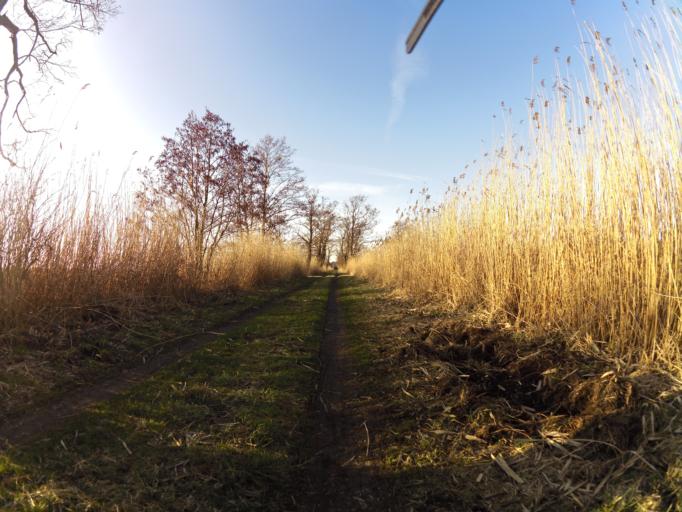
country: PL
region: West Pomeranian Voivodeship
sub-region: Powiat policki
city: Nowe Warpno
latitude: 53.7305
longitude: 14.3042
